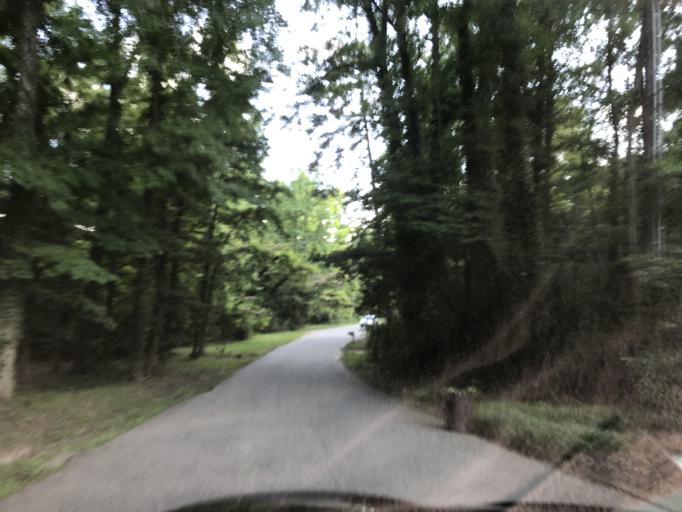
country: US
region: North Carolina
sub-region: Wake County
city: West Raleigh
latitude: 35.8128
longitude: -78.6724
